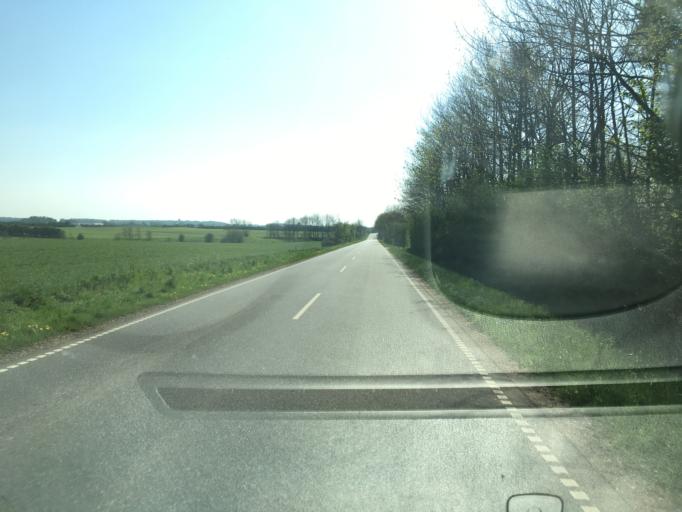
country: DK
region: South Denmark
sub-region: Haderslev Kommune
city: Vojens
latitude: 55.2989
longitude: 9.2529
